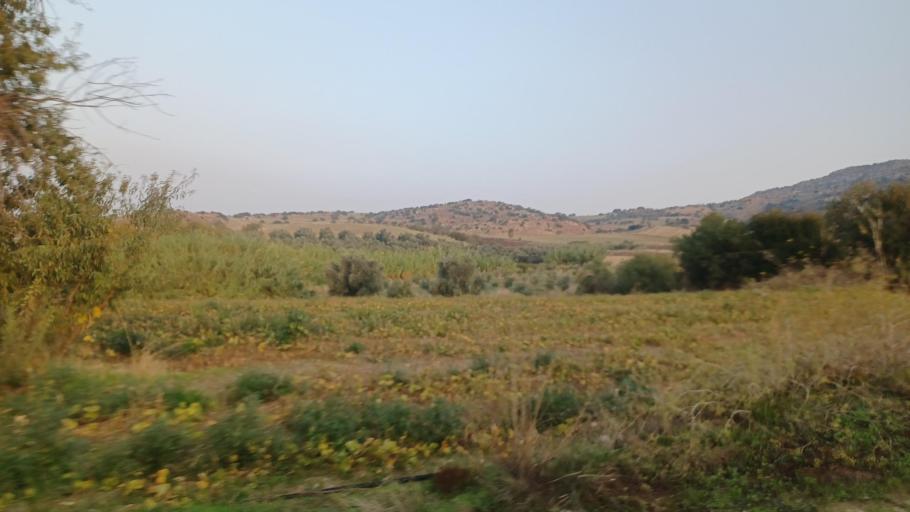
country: CY
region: Pafos
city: Polis
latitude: 34.9580
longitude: 32.4980
